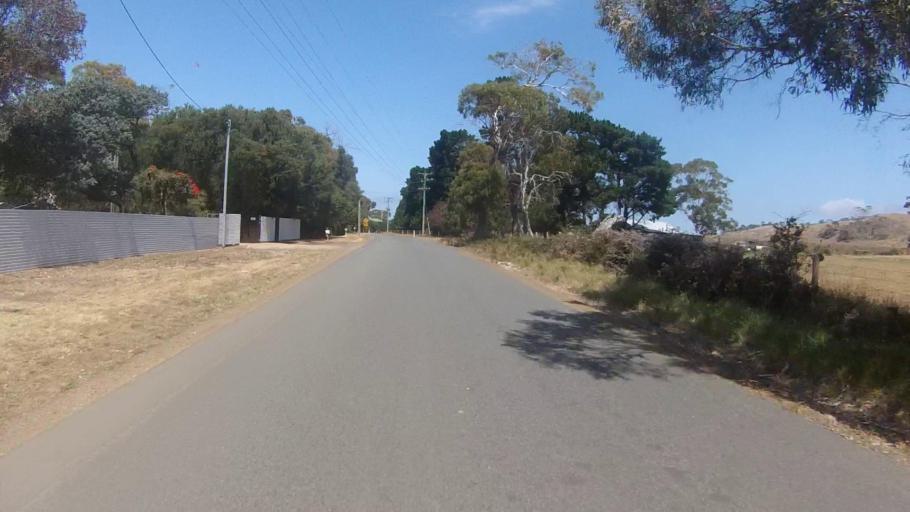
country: AU
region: Tasmania
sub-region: Sorell
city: Sorell
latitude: -42.8237
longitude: 147.8593
